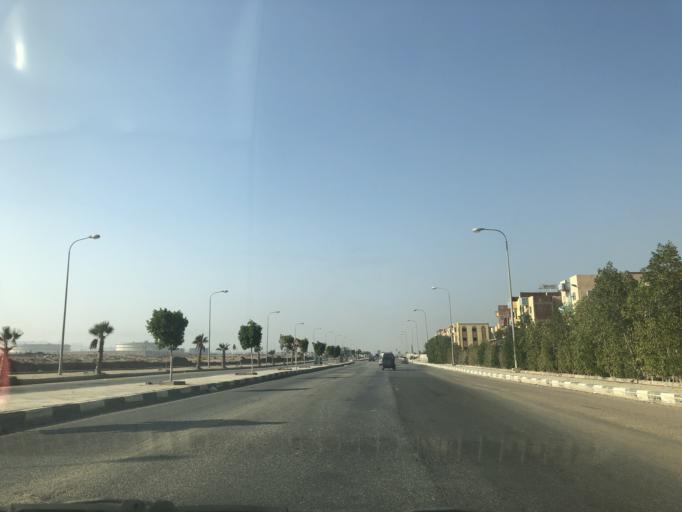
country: EG
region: Al Jizah
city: Madinat Sittah Uktubar
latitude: 29.9304
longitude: 31.0473
